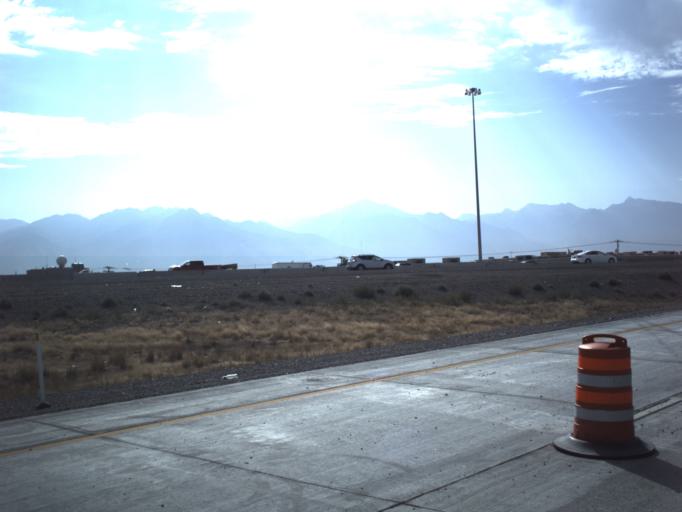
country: US
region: Utah
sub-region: Salt Lake County
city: West Valley City
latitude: 40.7232
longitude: -111.9532
